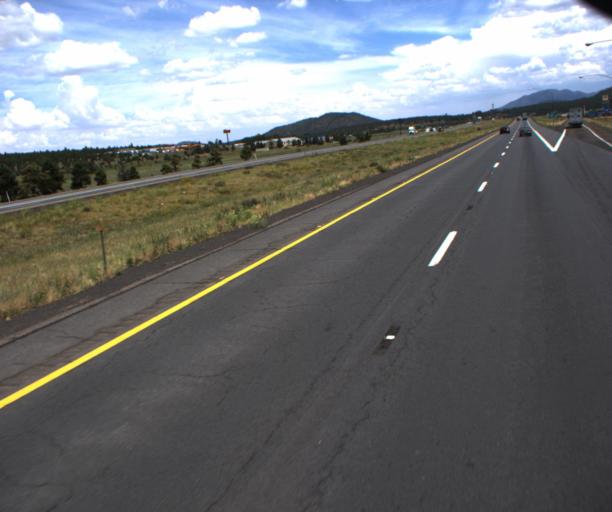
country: US
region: Arizona
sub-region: Coconino County
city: Williams
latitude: 35.2561
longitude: -112.1985
